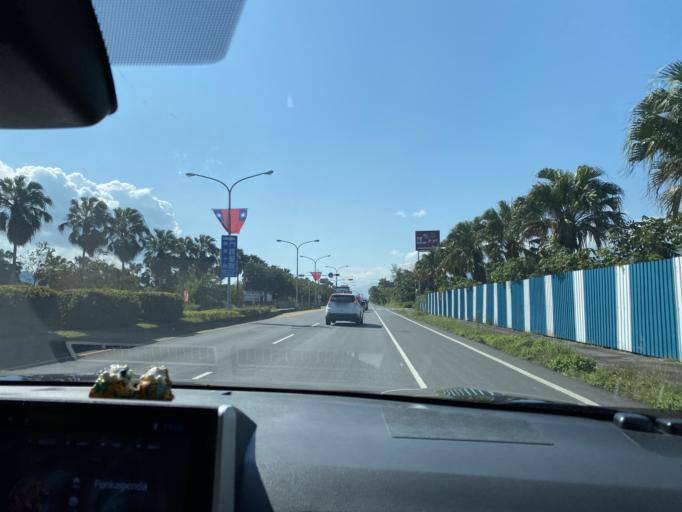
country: TW
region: Taiwan
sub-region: Hualien
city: Hualian
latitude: 23.8644
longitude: 121.5309
